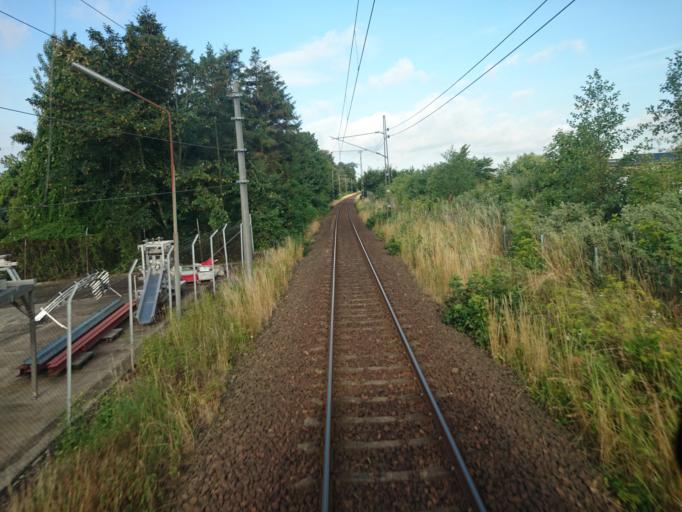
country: SE
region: Skane
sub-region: Ystads Kommun
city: Ystad
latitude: 55.4263
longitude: 13.8004
